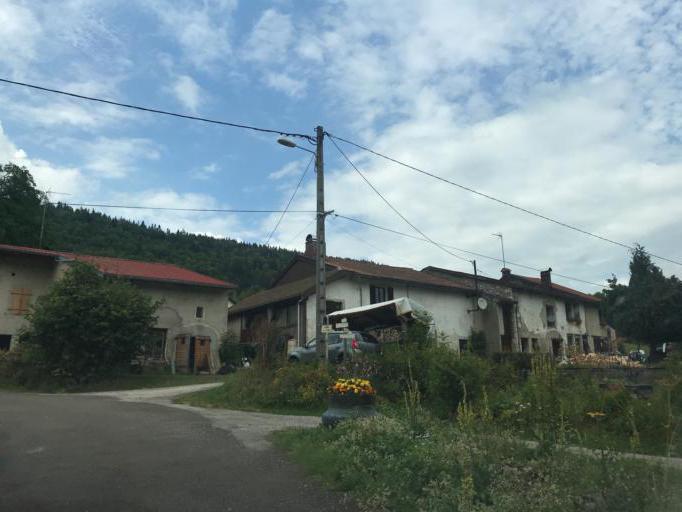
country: FR
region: Franche-Comte
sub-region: Departement du Jura
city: Longchaumois
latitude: 46.4732
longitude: 5.9001
